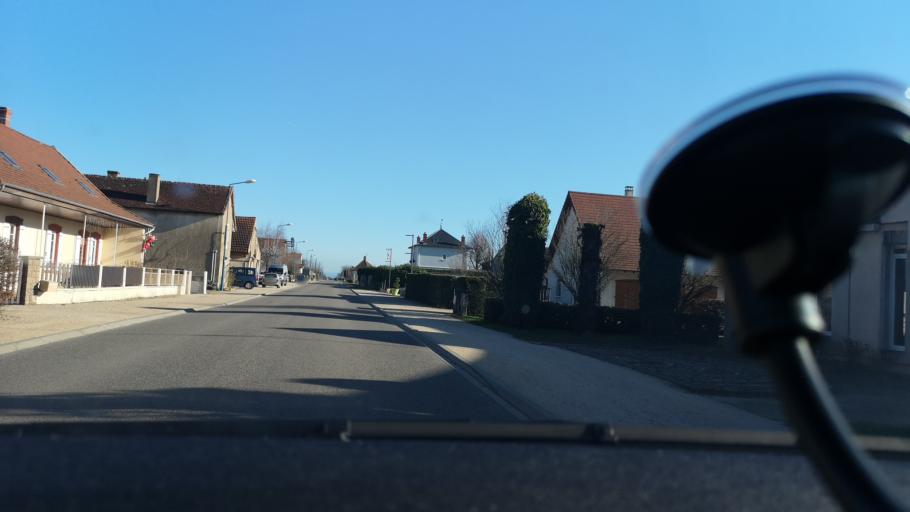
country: FR
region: Bourgogne
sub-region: Departement de Saone-et-Loire
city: Saint-Germain-du-Bois
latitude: 46.7523
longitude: 5.2496
